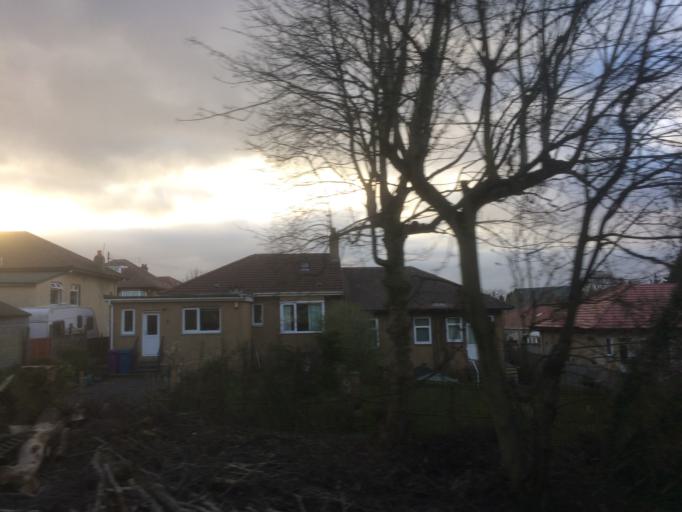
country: GB
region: Scotland
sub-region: East Renfrewshire
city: Giffnock
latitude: 55.8119
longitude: -4.2722
